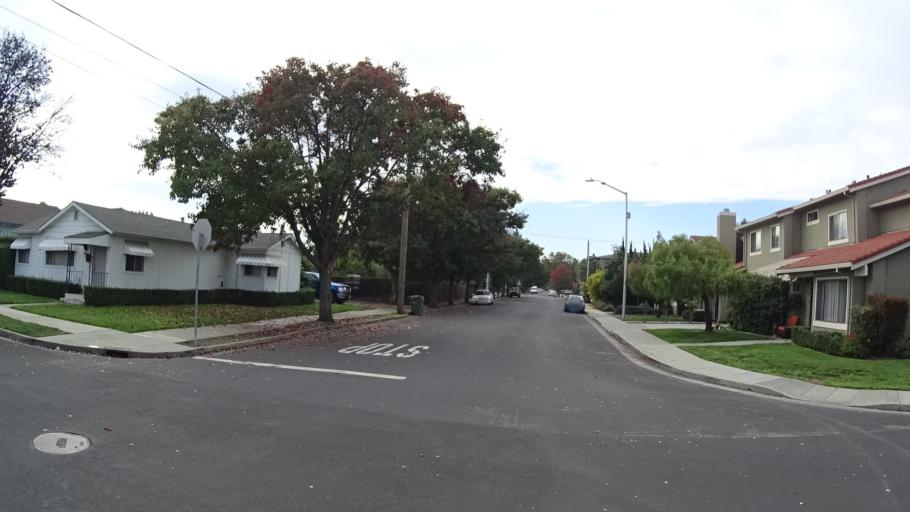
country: US
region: California
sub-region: Santa Clara County
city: Santa Clara
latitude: 37.3572
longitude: -121.9487
